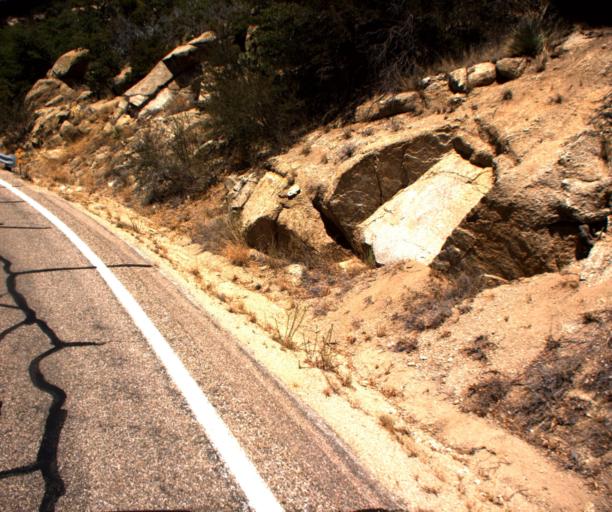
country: US
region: Arizona
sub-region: Pima County
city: Sells
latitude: 31.9600
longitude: -111.6248
